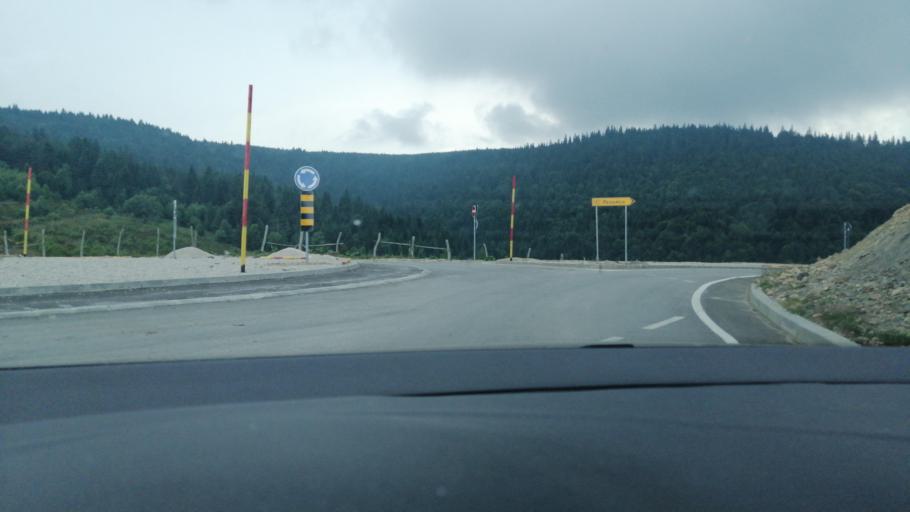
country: RS
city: Sokolovica
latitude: 43.3337
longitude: 20.2459
